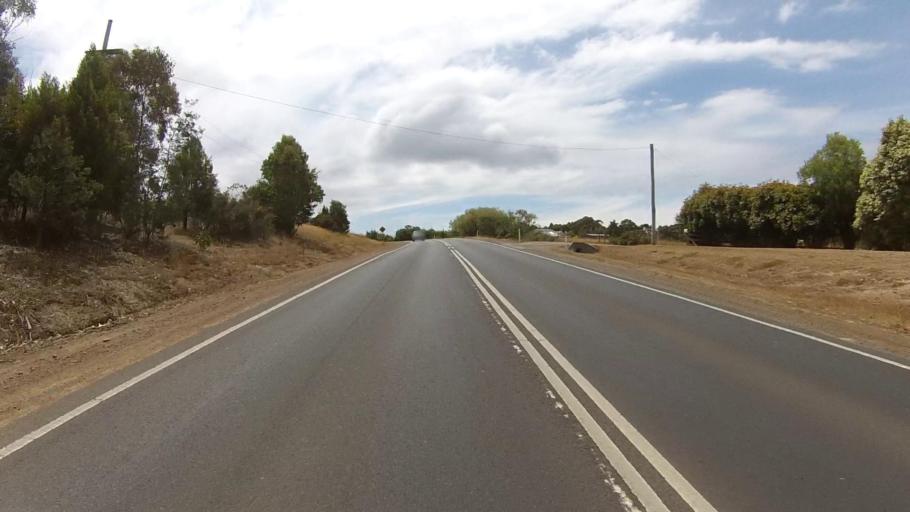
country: AU
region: Tasmania
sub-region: Kingborough
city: Margate
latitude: -43.0616
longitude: 147.2539
